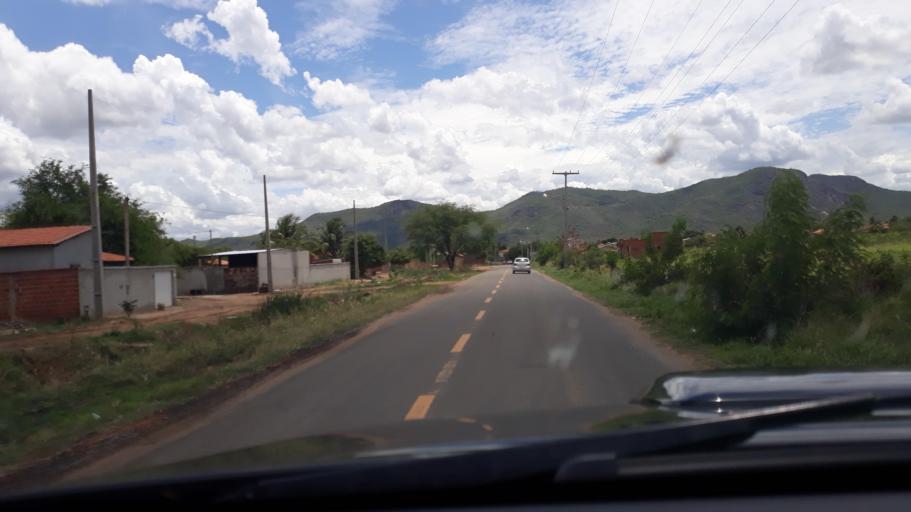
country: BR
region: Bahia
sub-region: Guanambi
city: Guanambi
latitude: -14.2804
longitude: -42.7129
